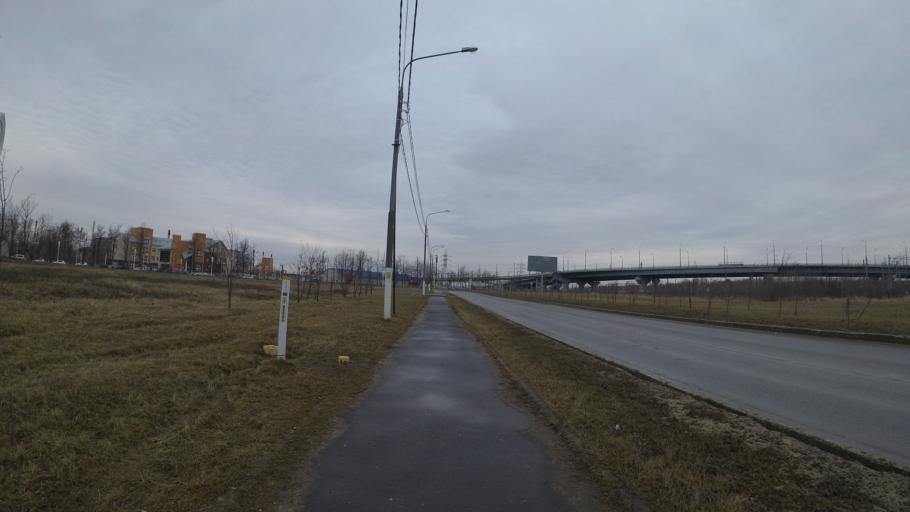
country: RU
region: Moskovskaya
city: Stupino
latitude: 54.8941
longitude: 38.0326
